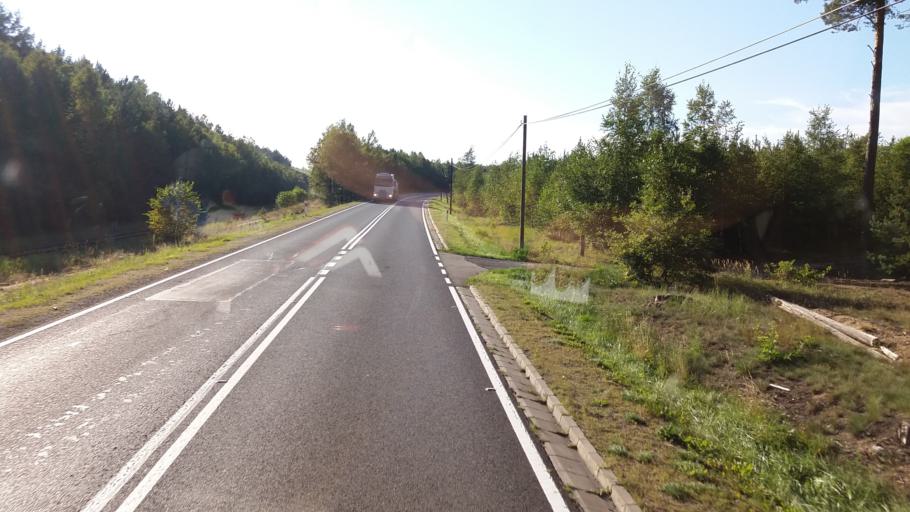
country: PL
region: West Pomeranian Voivodeship
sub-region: Powiat choszczenski
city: Drawno
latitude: 53.3023
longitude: 15.7927
